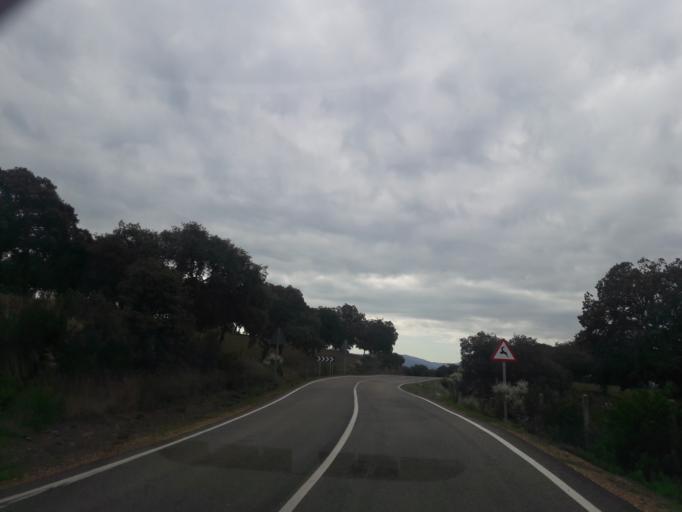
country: ES
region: Castille and Leon
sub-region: Provincia de Salamanca
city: Zamarra
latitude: 40.5444
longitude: -6.4197
